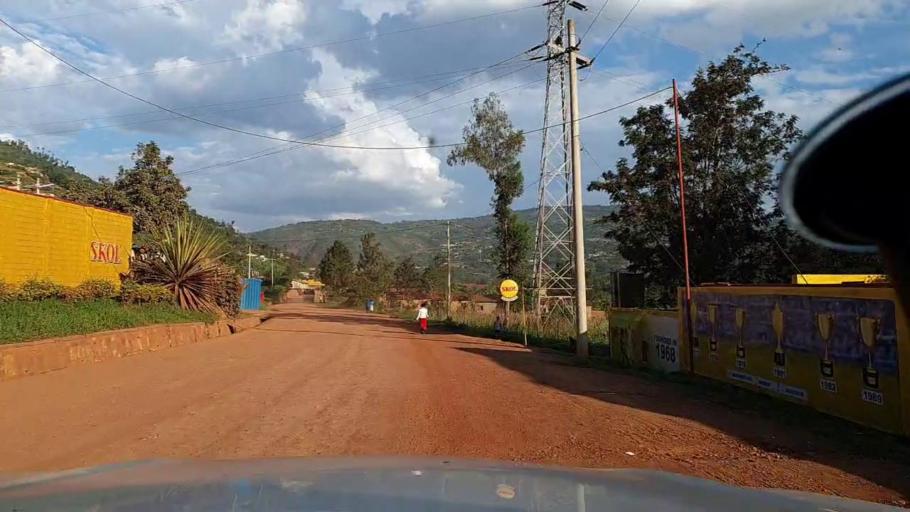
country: RW
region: Kigali
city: Kigali
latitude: -1.9437
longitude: 30.0044
